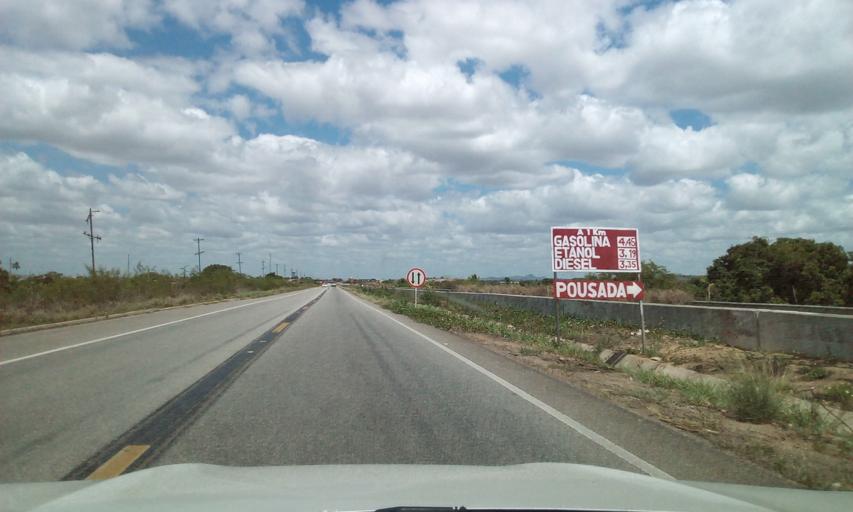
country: BR
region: Alagoas
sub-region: Porto Real Do Colegio
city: Porto Real do Colegio
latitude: -10.1956
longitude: -36.8229
